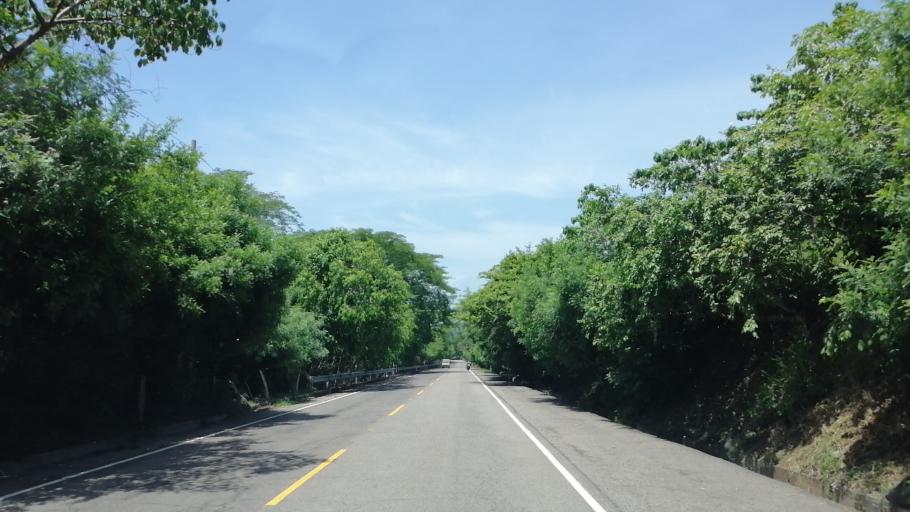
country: SV
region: Chalatenango
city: Nueva Concepcion
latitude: 14.1533
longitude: -89.3054
